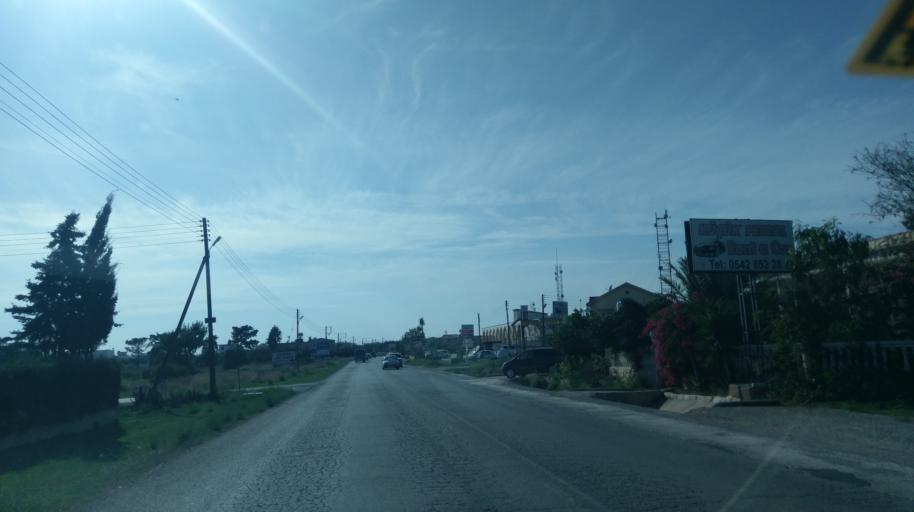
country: CY
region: Ammochostos
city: Trikomo
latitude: 35.2882
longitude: 33.9301
